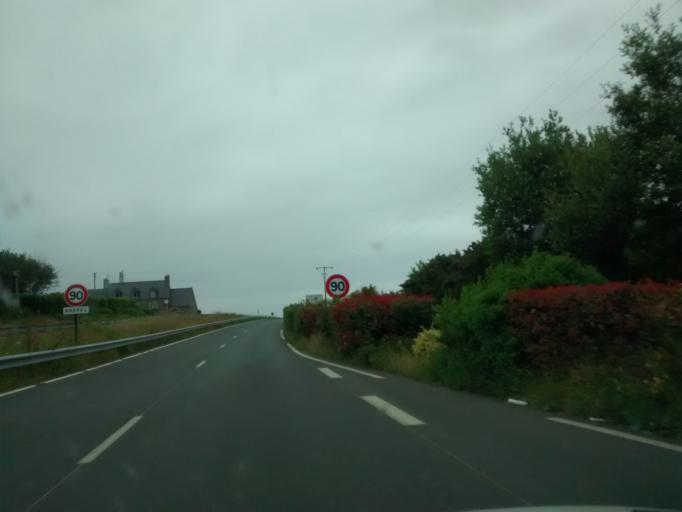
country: FR
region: Brittany
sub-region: Departement des Cotes-d'Armor
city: Saint-Quay-Perros
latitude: 48.7819
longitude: -3.4491
